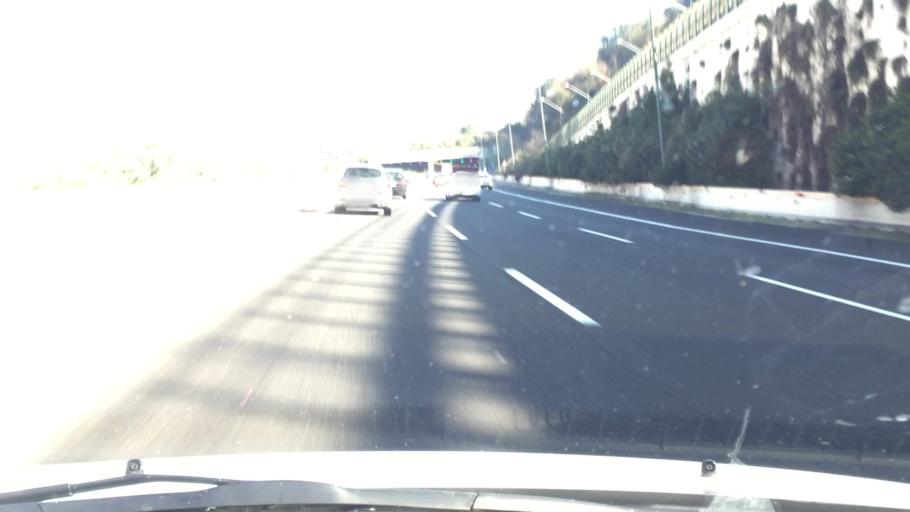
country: VA
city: Vatican City
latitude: 41.9787
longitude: 12.4290
